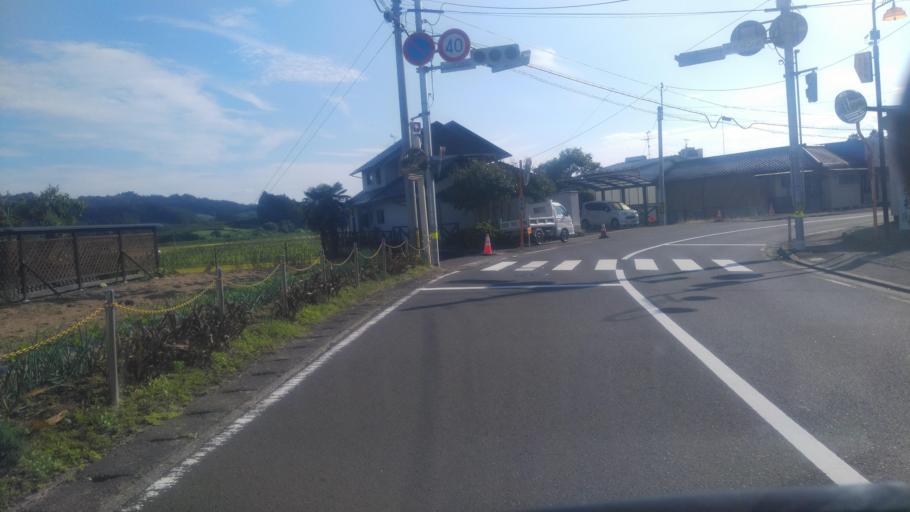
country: JP
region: Miyagi
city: Okawara
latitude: 38.1039
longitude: 140.6799
